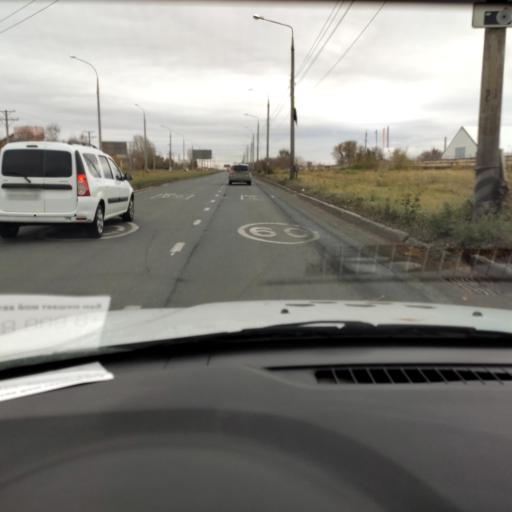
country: RU
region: Samara
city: Tol'yatti
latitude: 53.5583
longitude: 49.3211
